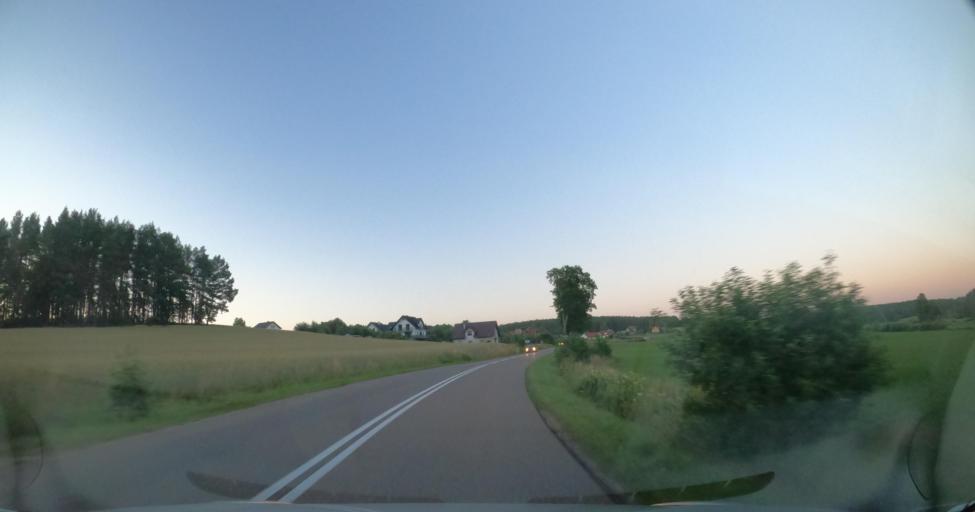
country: PL
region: Pomeranian Voivodeship
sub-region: Powiat wejherowski
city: Luzino
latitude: 54.4664
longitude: 18.0652
